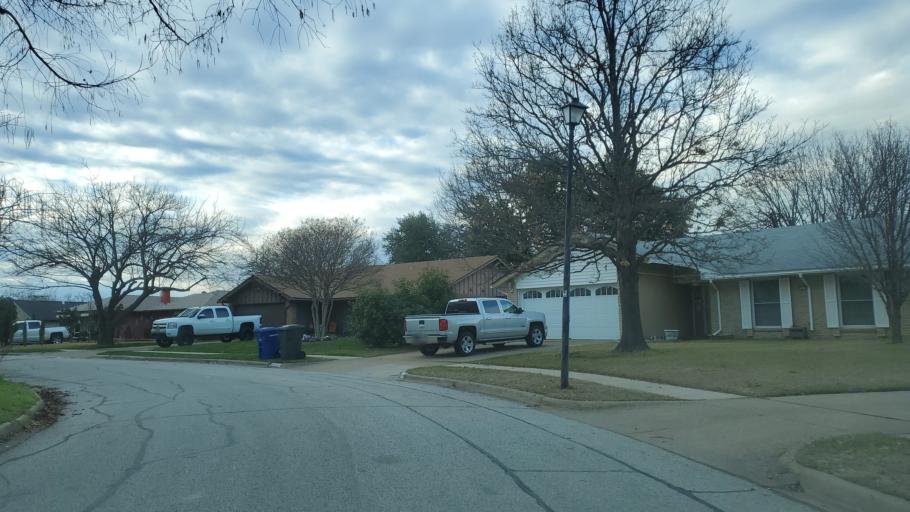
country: US
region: Texas
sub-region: Dallas County
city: Carrollton
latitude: 32.9869
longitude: -96.8825
